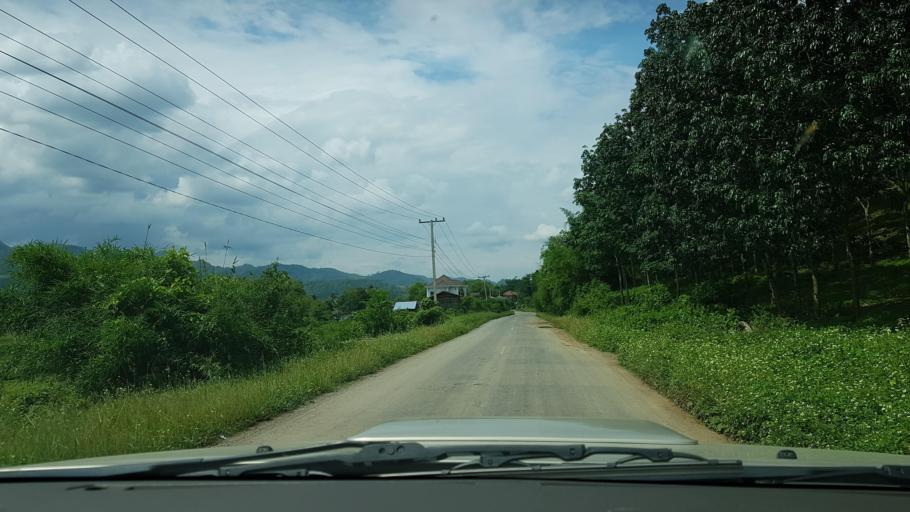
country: LA
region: Loungnamtha
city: Muang Nale
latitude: 20.2621
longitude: 101.5934
